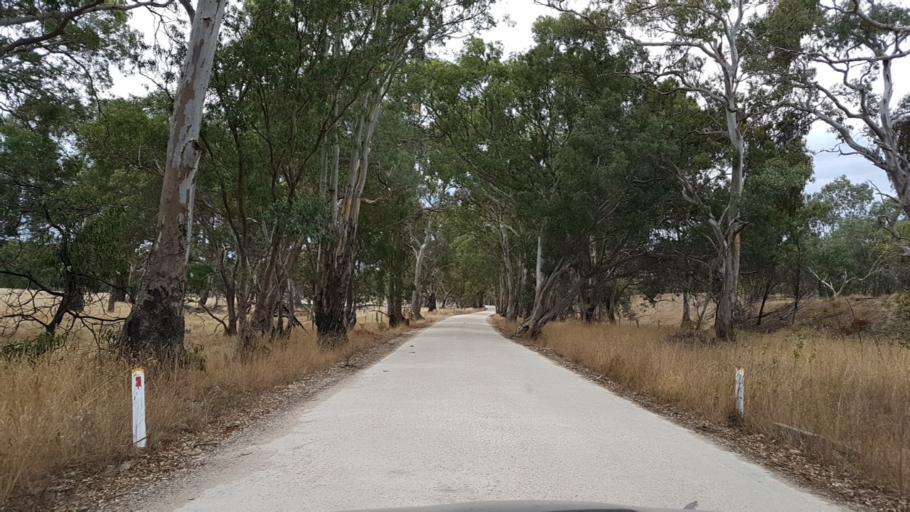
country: AU
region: South Australia
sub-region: Adelaide Hills
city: Birdwood
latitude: -34.7912
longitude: 138.9707
